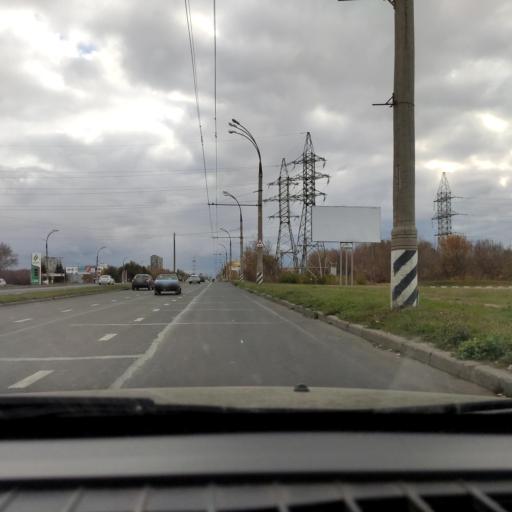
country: RU
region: Samara
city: Tol'yatti
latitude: 53.5479
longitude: 49.2655
